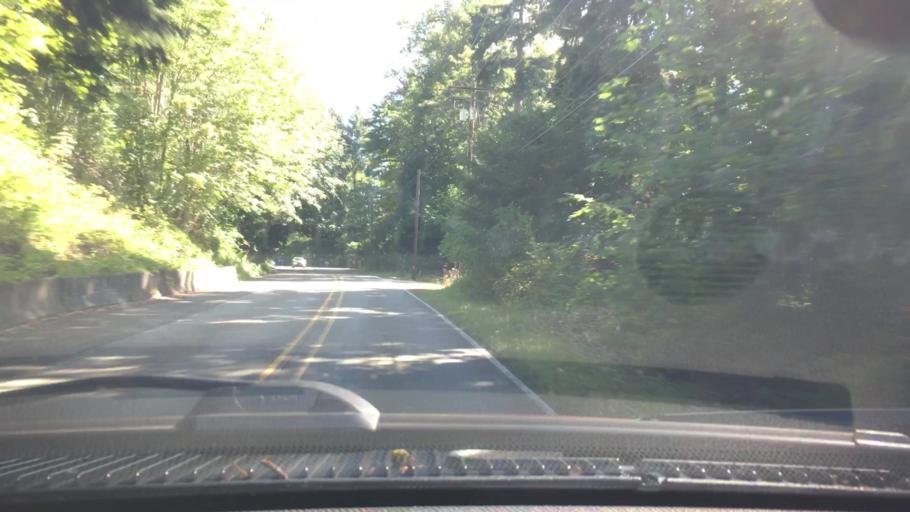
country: US
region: Washington
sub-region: King County
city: Sammamish
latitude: 47.6199
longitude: -122.0954
